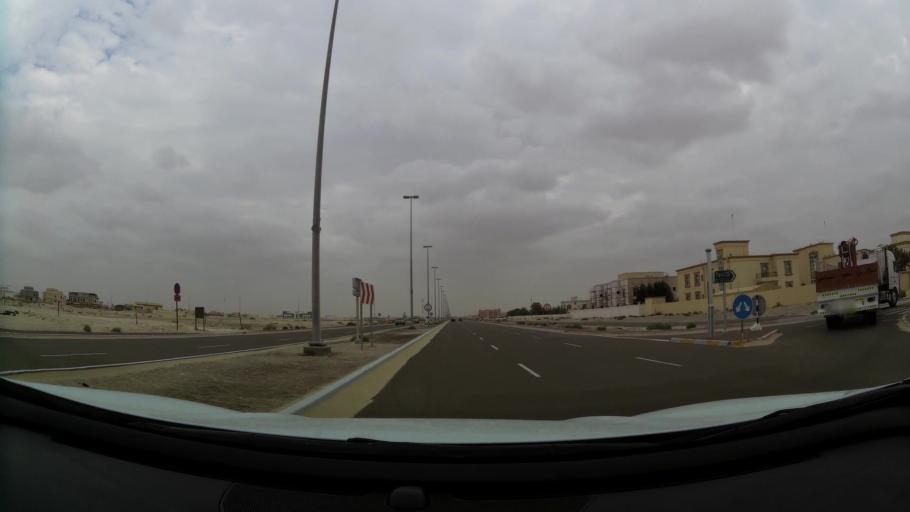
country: AE
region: Abu Dhabi
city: Abu Dhabi
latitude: 24.3667
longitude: 54.6269
